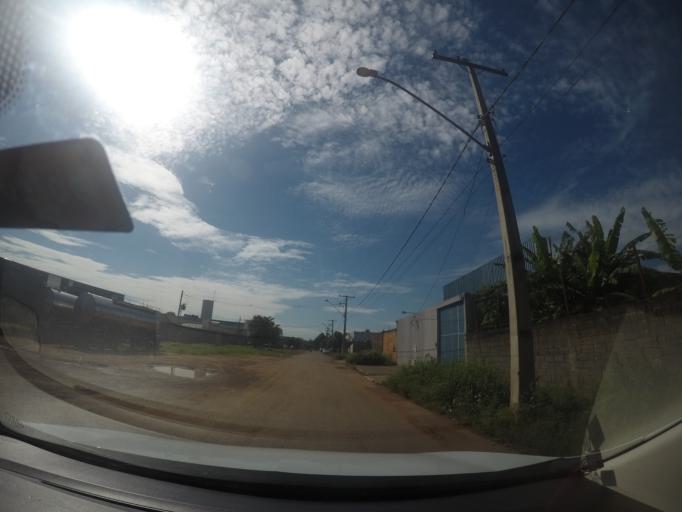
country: BR
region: Goias
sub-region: Goiania
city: Goiania
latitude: -16.6602
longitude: -49.2090
